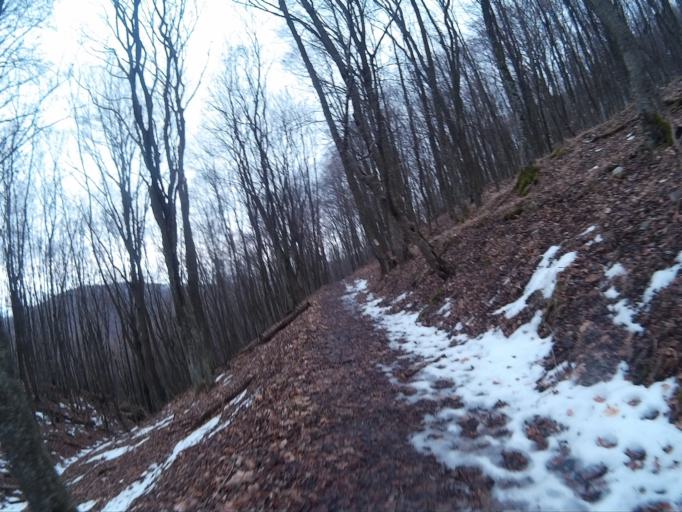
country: HU
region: Heves
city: Belapatfalva
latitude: 48.0559
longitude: 20.4034
